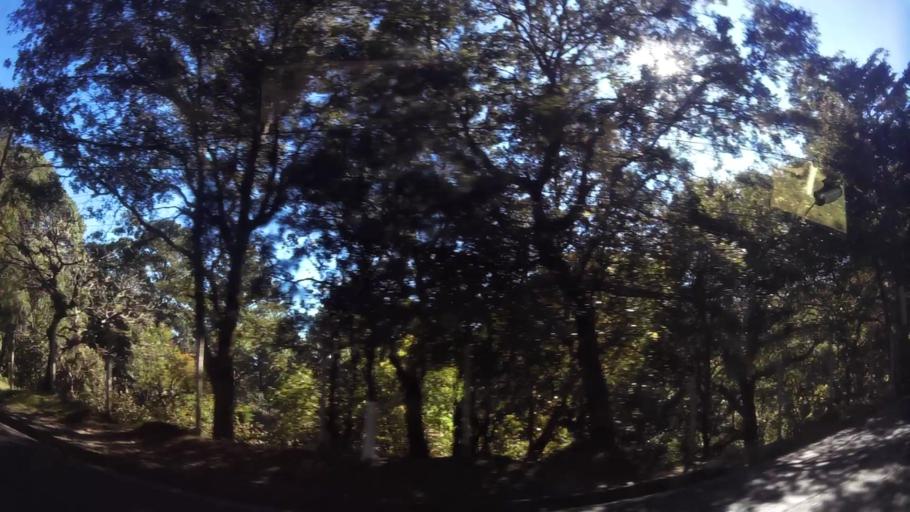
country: GT
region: Guatemala
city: Fraijanes
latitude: 14.4763
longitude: -90.4538
